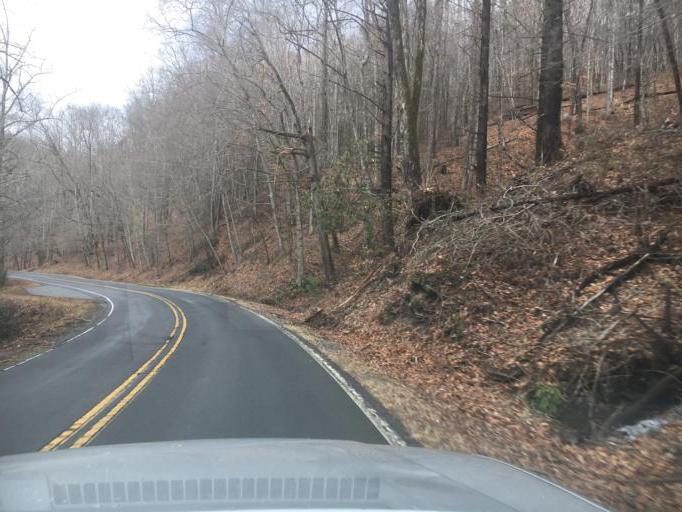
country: US
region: North Carolina
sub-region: Transylvania County
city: Brevard
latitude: 35.2882
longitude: -82.7608
